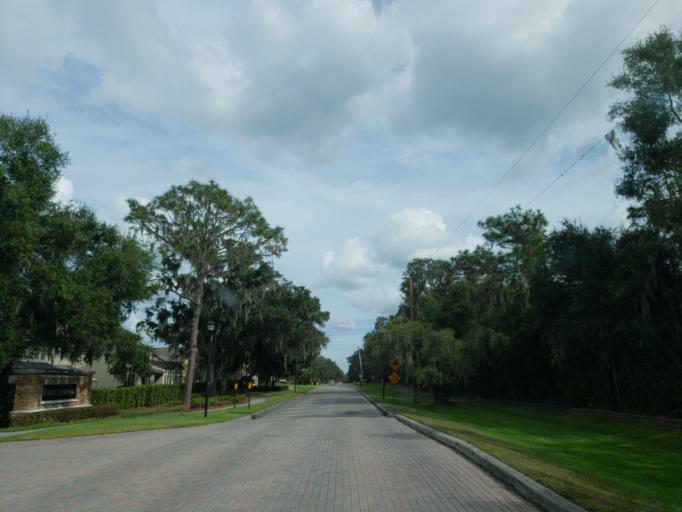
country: US
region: Florida
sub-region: Hillsborough County
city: Fish Hawk
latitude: 27.8428
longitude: -82.2077
